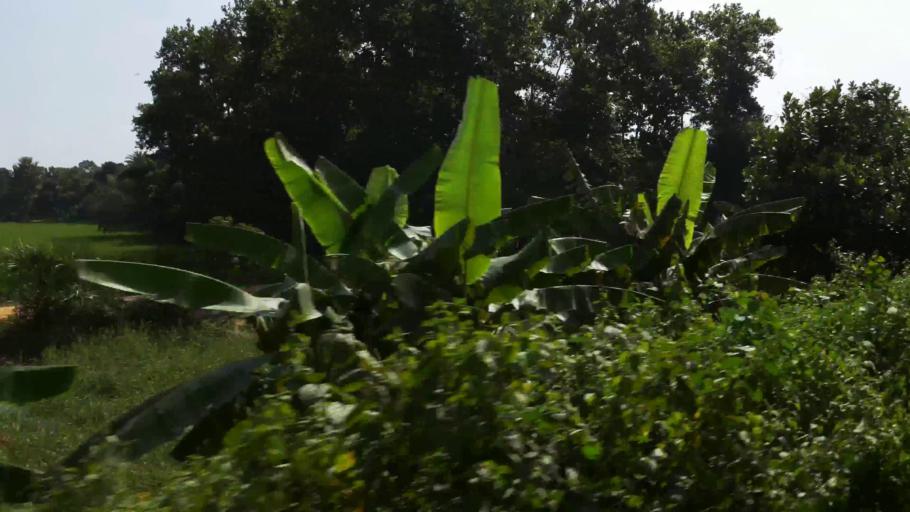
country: BD
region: Dhaka
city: Tungi
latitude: 24.1531
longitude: 90.4658
